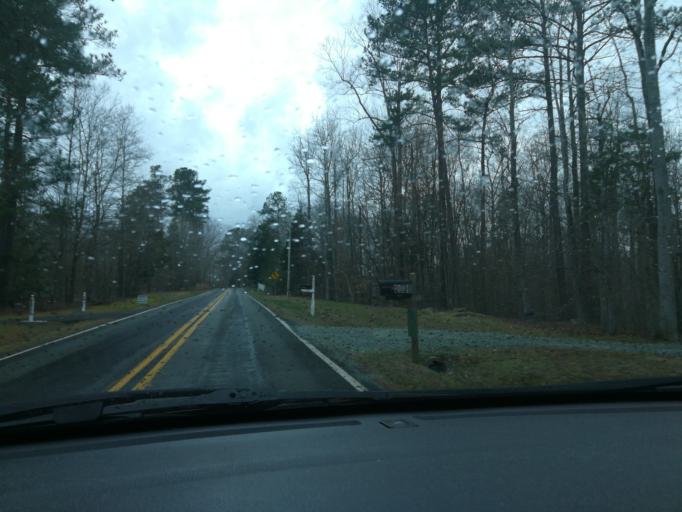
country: US
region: North Carolina
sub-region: Orange County
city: Hillsborough
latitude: 36.0227
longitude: -79.0653
